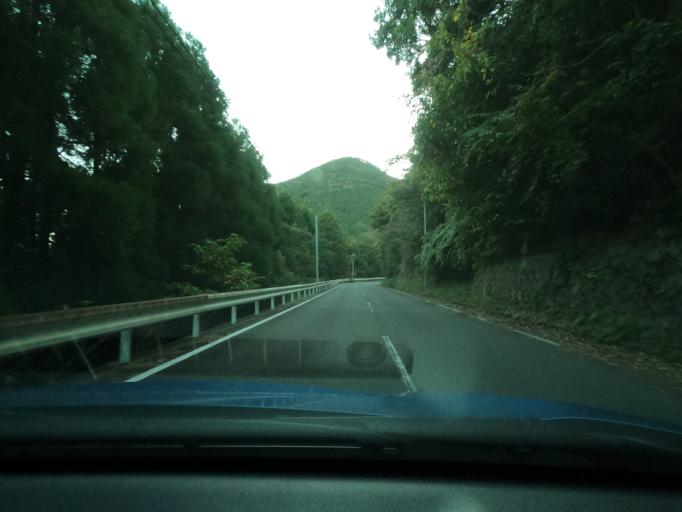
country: JP
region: Kagoshima
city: Satsumasendai
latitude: 31.8162
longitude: 130.4760
